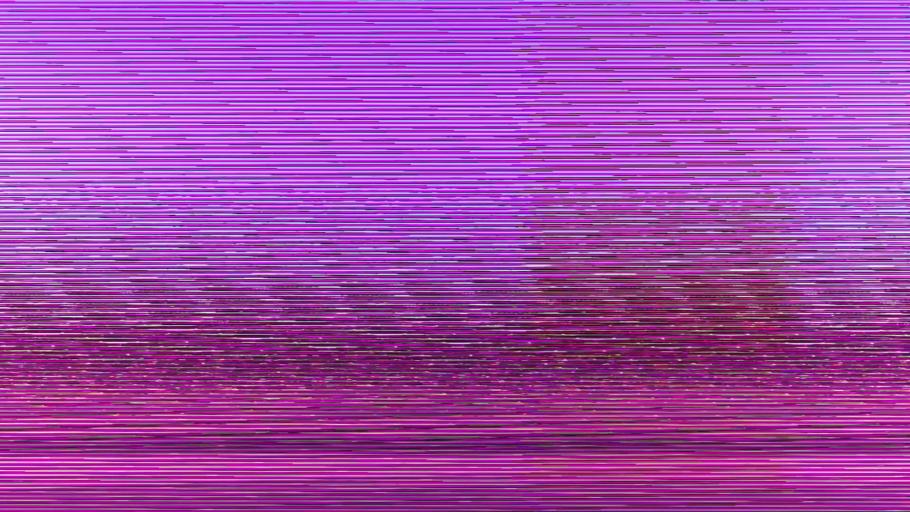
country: US
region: Michigan
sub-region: Oakland County
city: Troy
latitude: 42.5903
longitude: -83.1685
